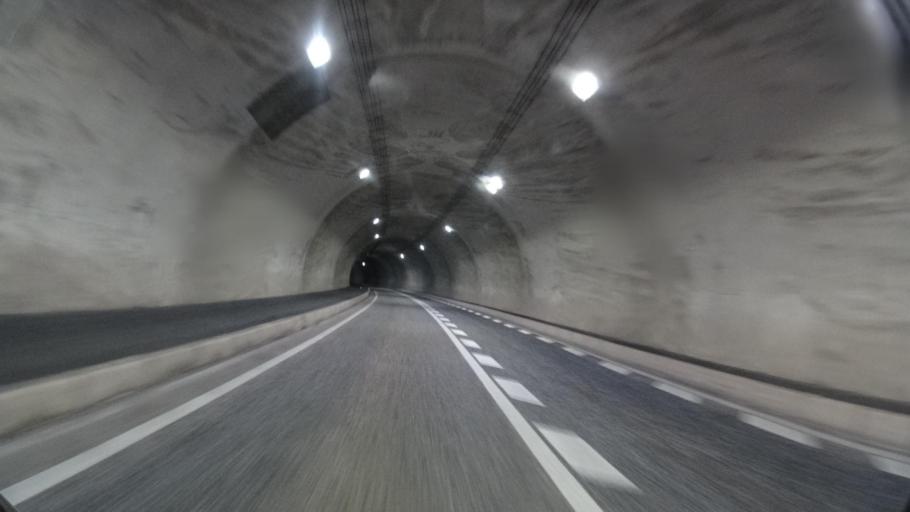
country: JP
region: Kyoto
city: Maizuru
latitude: 35.5354
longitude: 135.3477
